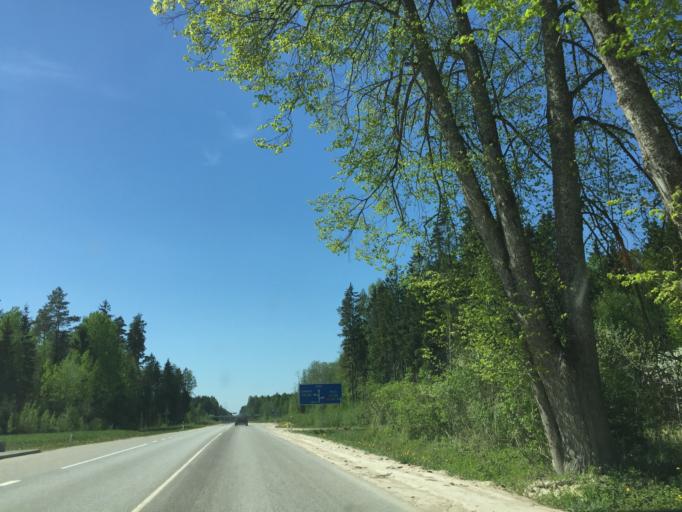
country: LV
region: Ogre
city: Ogre
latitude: 56.8486
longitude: 24.6826
